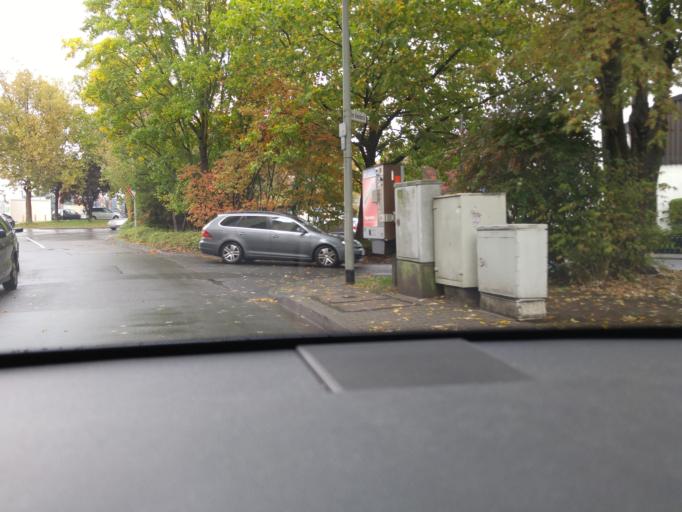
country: DE
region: Hesse
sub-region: Regierungsbezirk Darmstadt
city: Hattersheim
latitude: 50.0709
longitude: 8.4770
